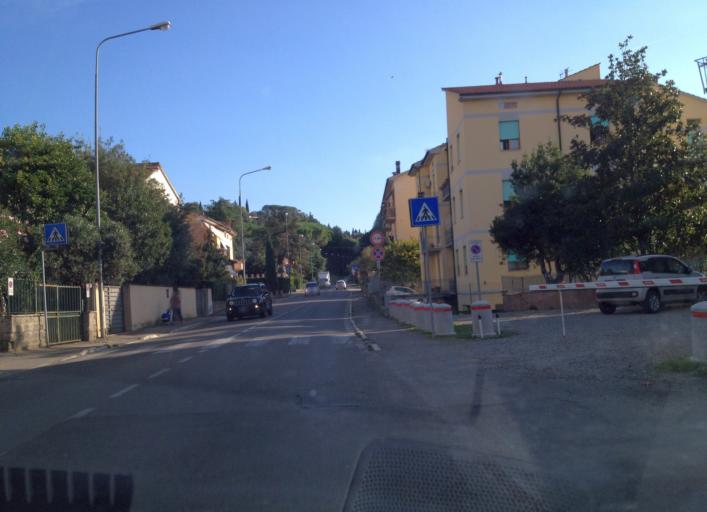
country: IT
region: Tuscany
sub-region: Provincia di Siena
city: Poggibonsi
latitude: 43.4668
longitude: 11.1441
